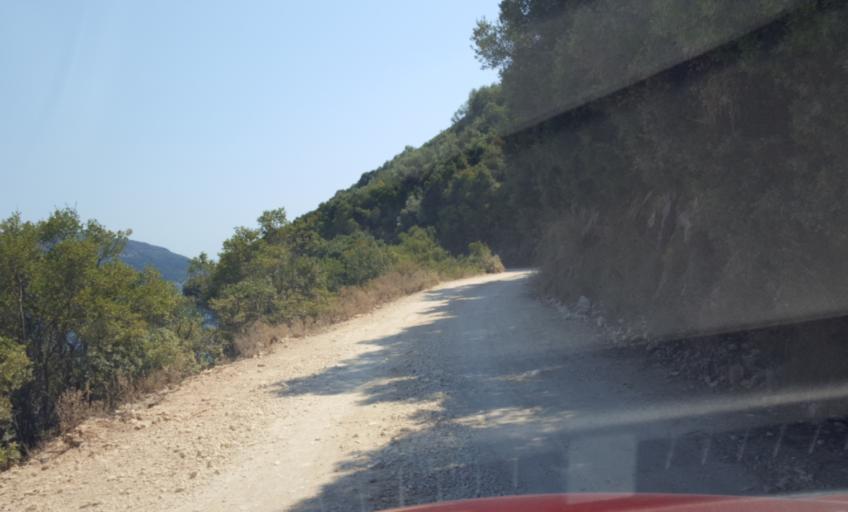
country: GR
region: Ionian Islands
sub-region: Lefkada
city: Nidri
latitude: 38.6625
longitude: 20.7150
